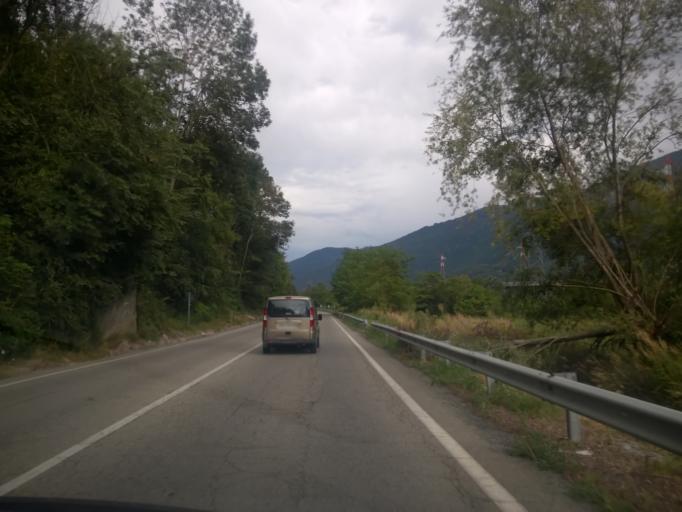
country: IT
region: Piedmont
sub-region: Provincia di Torino
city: Sant'Antonino di Susa
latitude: 45.1133
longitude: 7.2608
